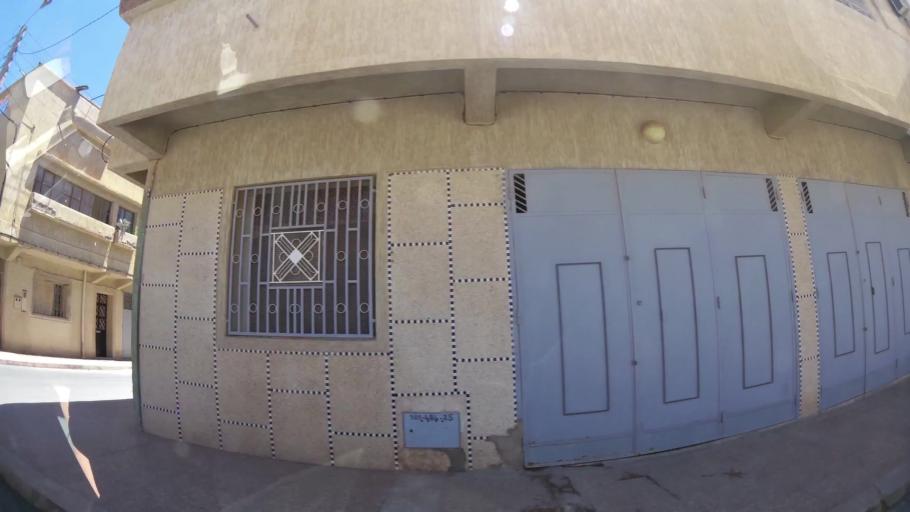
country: MA
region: Oriental
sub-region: Oujda-Angad
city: Oujda
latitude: 34.6779
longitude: -1.8764
